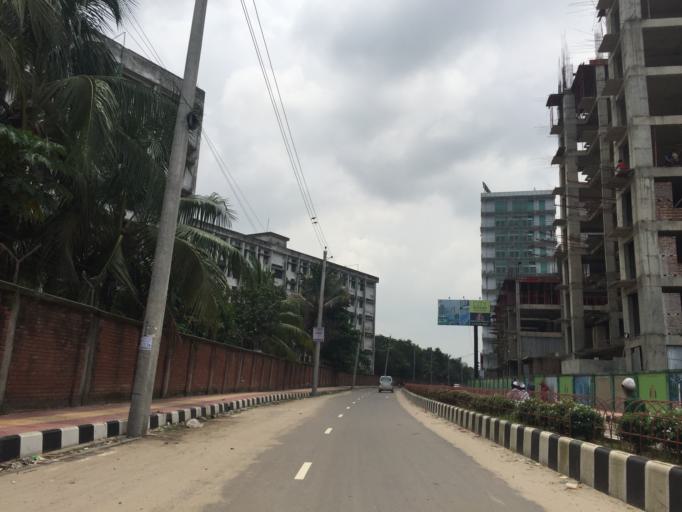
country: BD
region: Dhaka
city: Paltan
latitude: 23.8040
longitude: 90.3842
